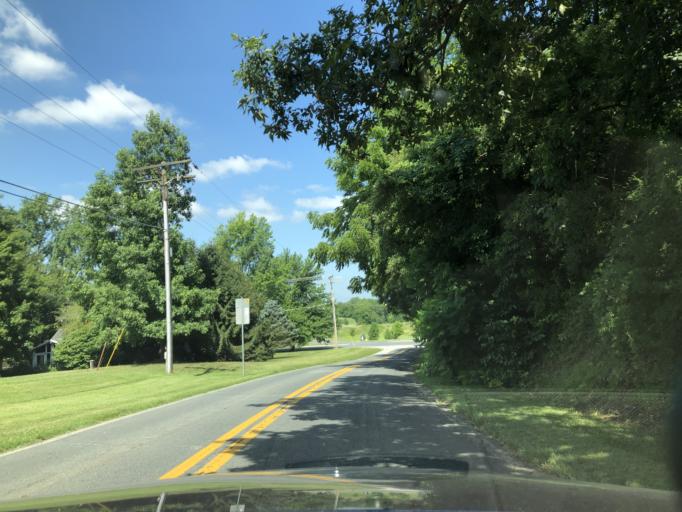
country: US
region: Maryland
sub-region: Carroll County
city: Westminster
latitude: 39.6047
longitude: -76.9716
